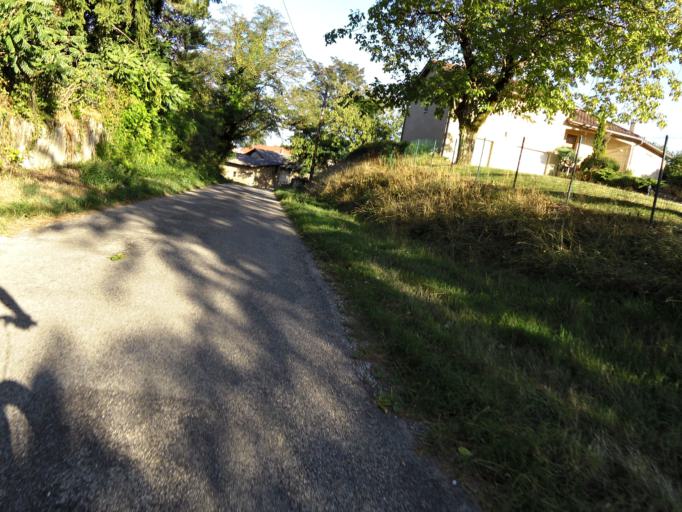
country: FR
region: Rhone-Alpes
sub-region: Departement de l'Ain
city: Perouges
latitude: 45.9082
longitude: 5.1726
